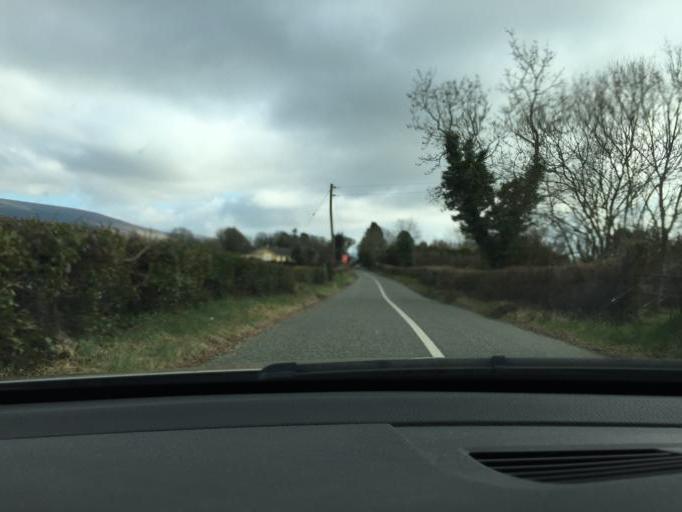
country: IE
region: Leinster
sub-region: Wicklow
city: Valleymount
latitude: 53.1103
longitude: -6.5272
